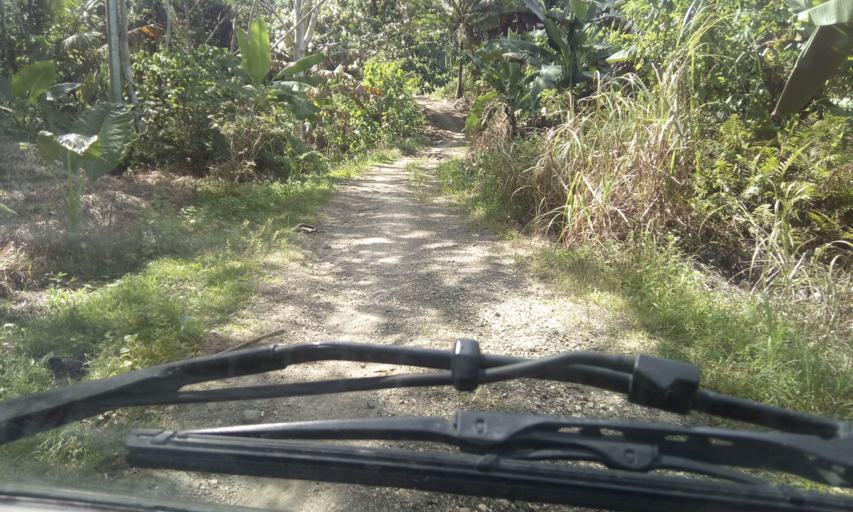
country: PH
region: Caraga
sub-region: Province of Agusan del Sur
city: Santa Josefa
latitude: 7.9547
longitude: 125.9862
